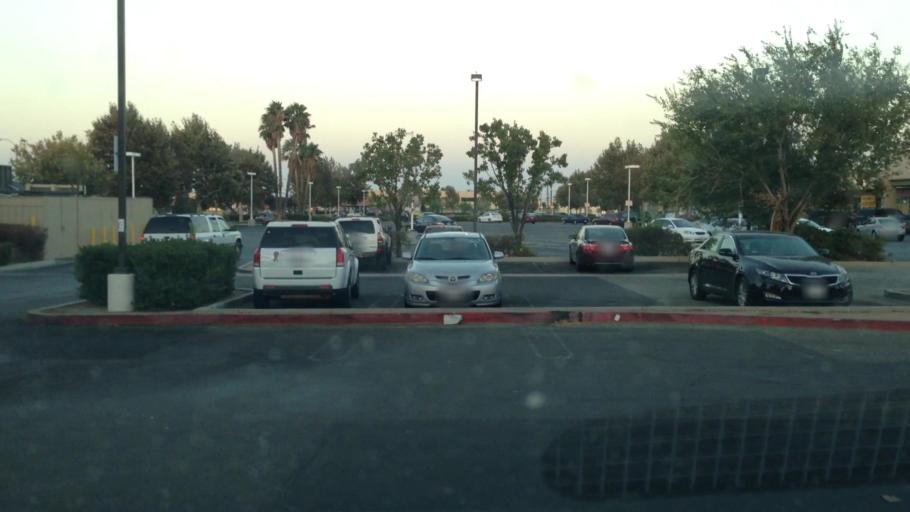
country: US
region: California
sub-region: Los Angeles County
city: Palmdale
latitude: 34.5793
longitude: -118.1278
